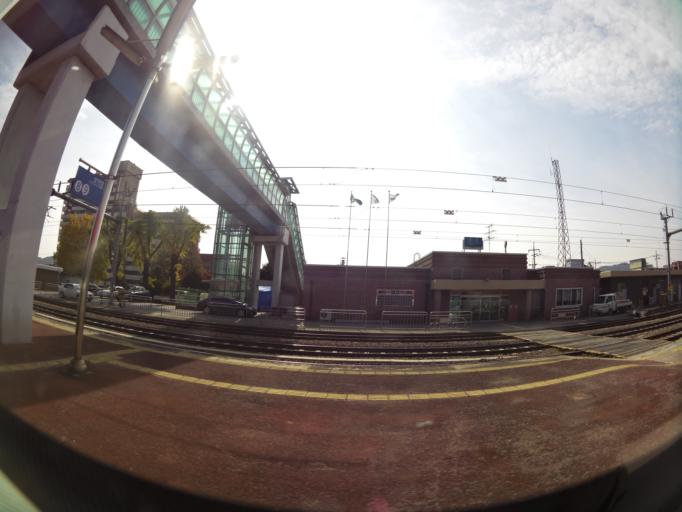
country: KR
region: Daejeon
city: Sintansin
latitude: 36.5323
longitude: 127.3658
